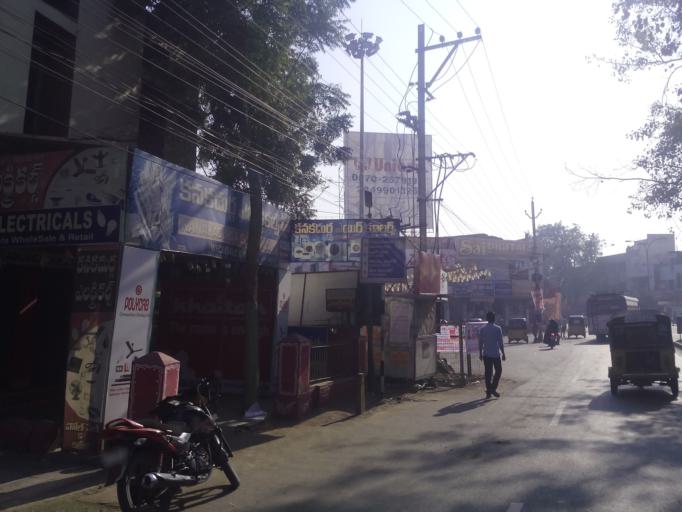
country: IN
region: Telangana
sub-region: Warangal
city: Warangal
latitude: 17.9897
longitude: 79.5964
